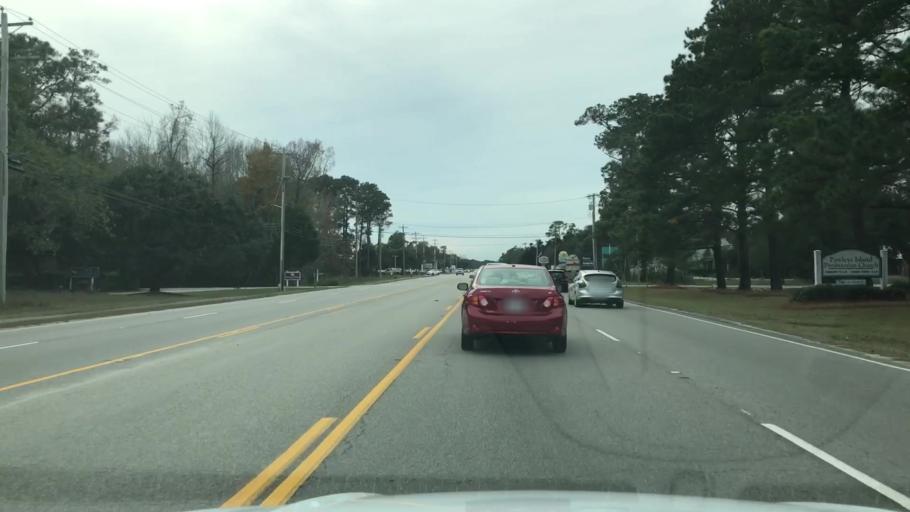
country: US
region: South Carolina
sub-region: Georgetown County
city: Murrells Inlet
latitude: 33.4351
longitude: -79.1348
